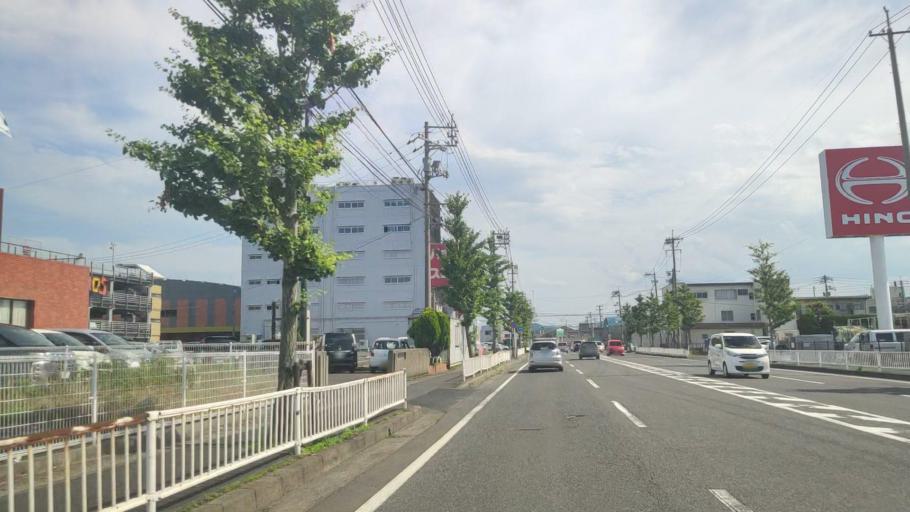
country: JP
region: Tottori
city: Tottori
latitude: 35.5158
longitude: 134.1921
